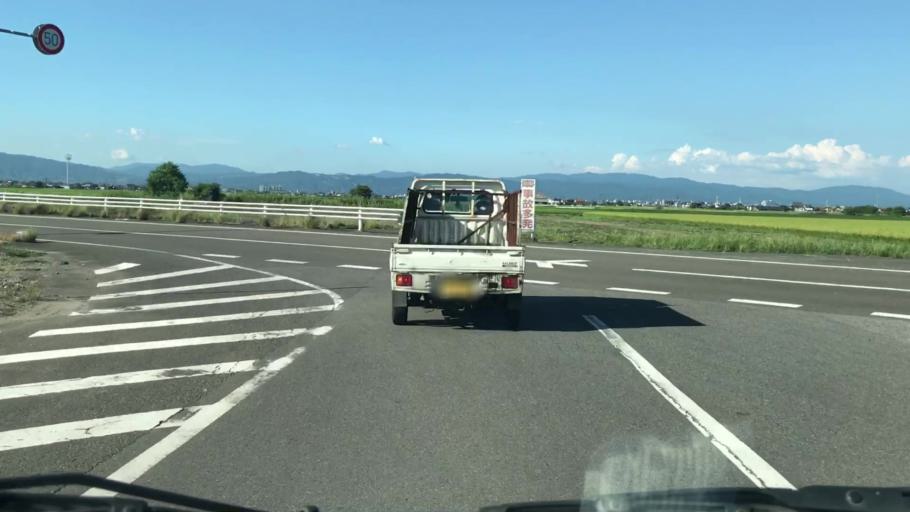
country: JP
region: Saga Prefecture
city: Saga-shi
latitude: 33.2070
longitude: 130.2686
